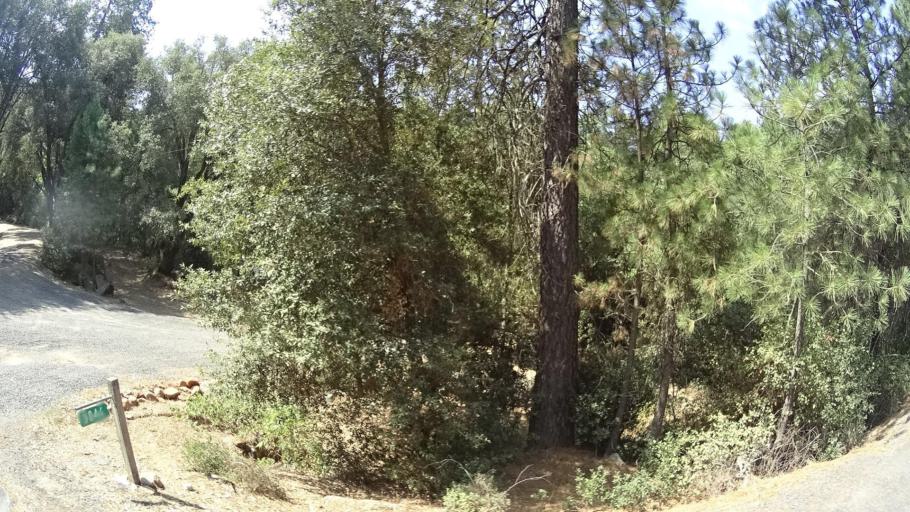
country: US
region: California
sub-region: Mariposa County
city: Midpines
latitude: 37.6998
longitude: -120.1342
